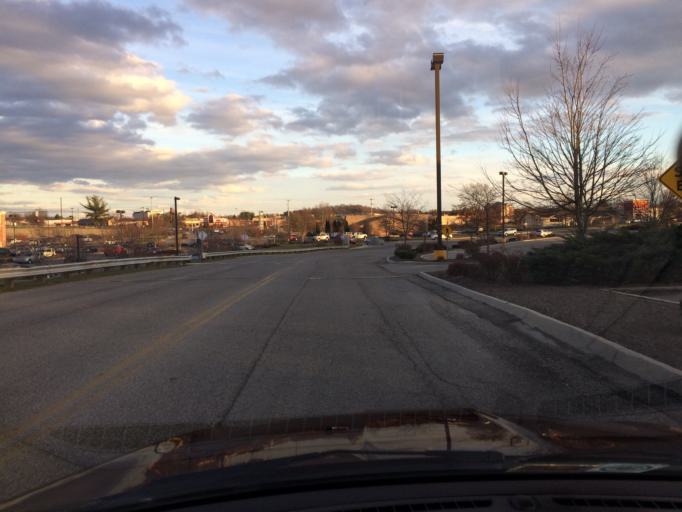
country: US
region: Virginia
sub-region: Montgomery County
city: Merrimac
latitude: 37.1669
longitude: -80.4258
